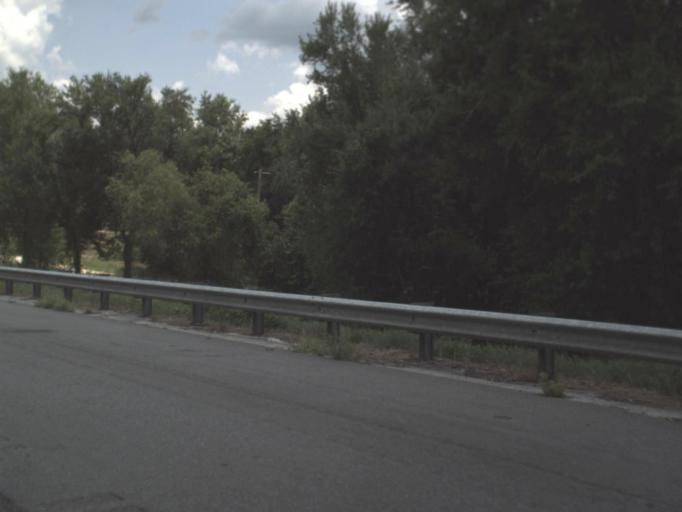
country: US
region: Florida
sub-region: Suwannee County
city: Wellborn
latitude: 30.3642
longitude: -82.8523
